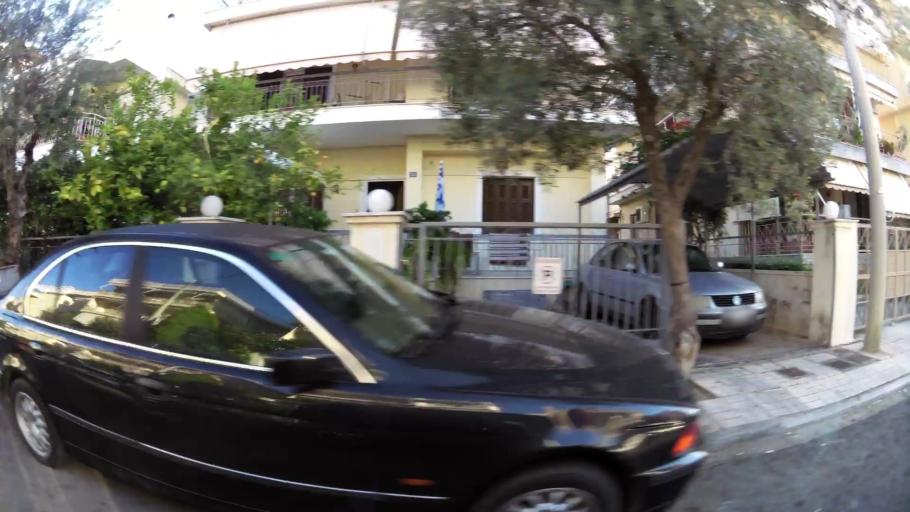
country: GR
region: Attica
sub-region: Nomarchia Athinas
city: Argyroupoli
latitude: 37.8863
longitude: 23.7586
